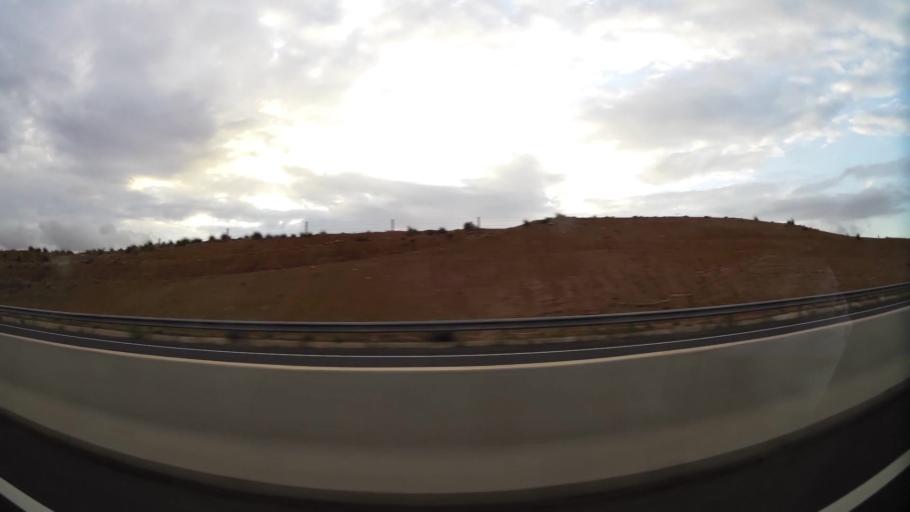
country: MA
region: Oriental
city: Taourirt
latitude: 34.4521
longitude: -3.0490
